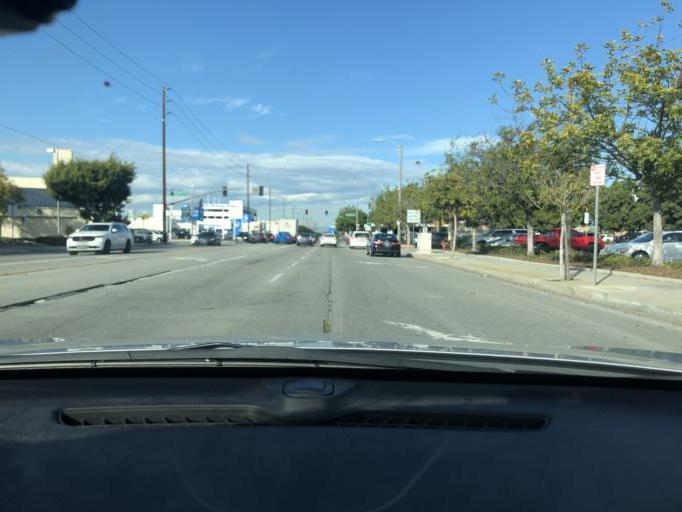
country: US
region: California
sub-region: Los Angeles County
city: Gardena
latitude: 33.8876
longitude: -118.3091
